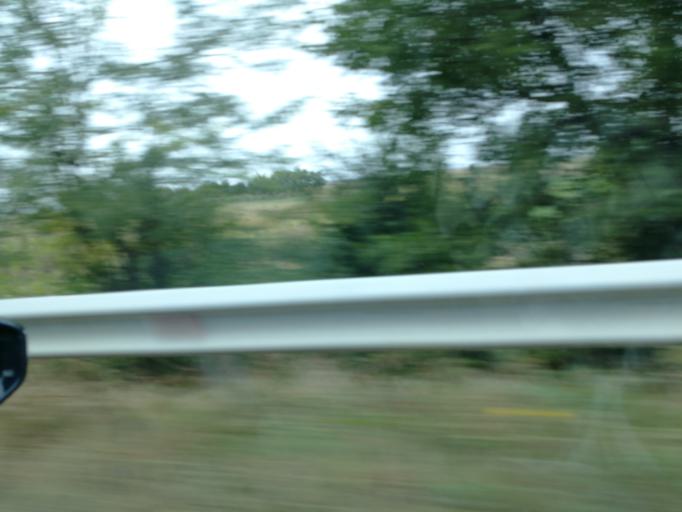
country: RO
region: Tulcea
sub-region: Oras Macin
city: Macin
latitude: 45.2594
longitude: 28.0771
